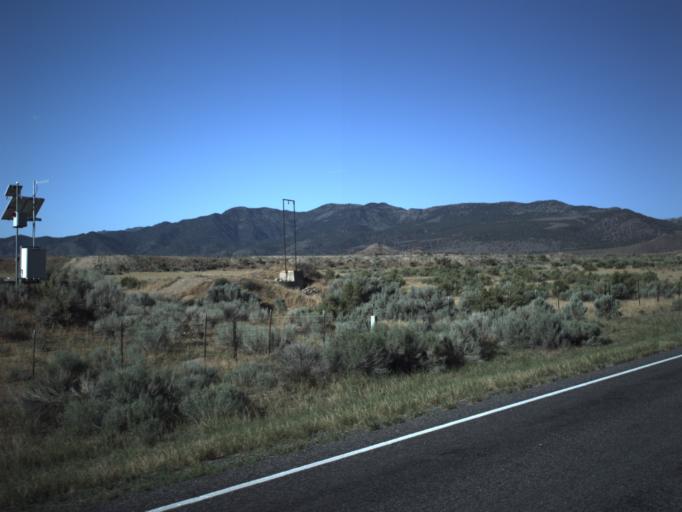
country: US
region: Utah
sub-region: Utah County
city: Genola
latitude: 39.9518
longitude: -111.9770
